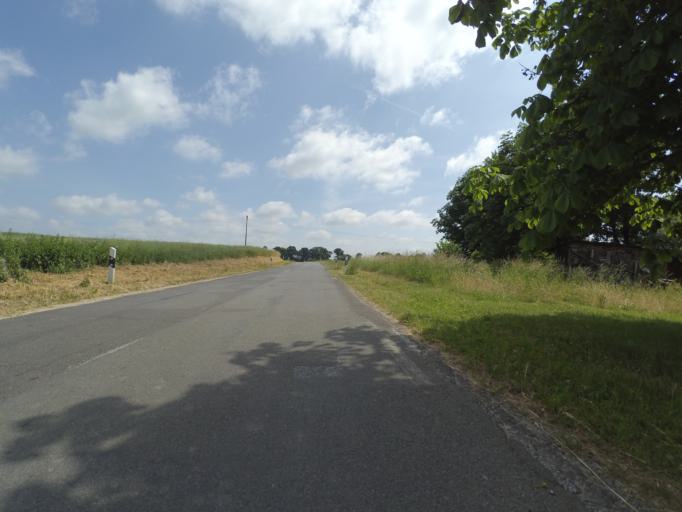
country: DE
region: Mecklenburg-Vorpommern
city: Neuburg
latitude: 53.4412
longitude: 11.9516
